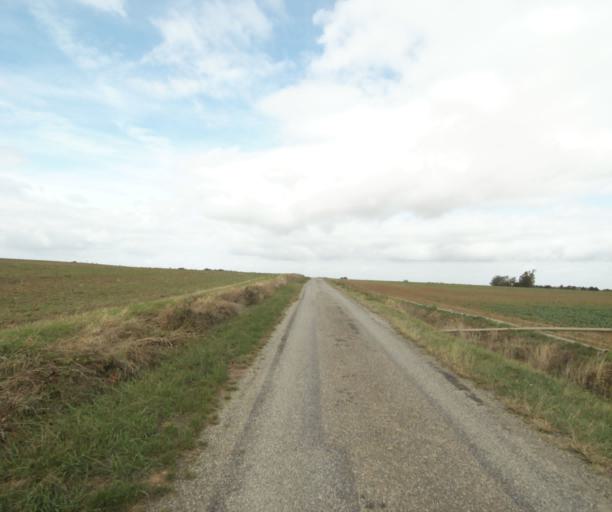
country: FR
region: Midi-Pyrenees
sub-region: Departement du Tarn-et-Garonne
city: Beaumont-de-Lomagne
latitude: 43.8688
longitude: 1.0890
